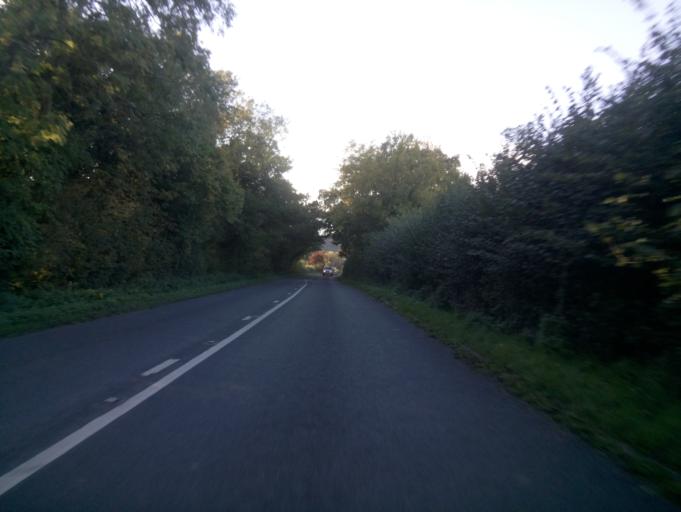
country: GB
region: England
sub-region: Worcestershire
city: Great Malvern
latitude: 52.0182
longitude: -2.3208
